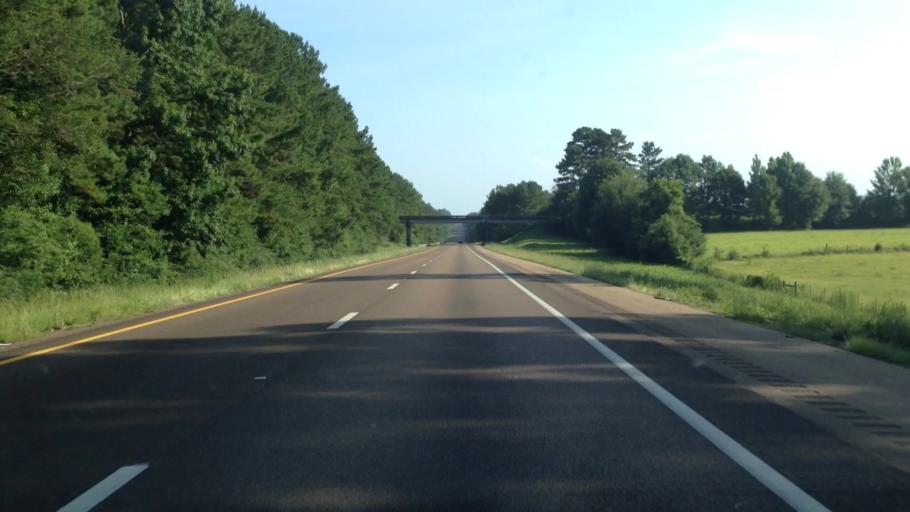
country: US
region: Mississippi
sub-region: Pike County
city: Summit
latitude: 31.3871
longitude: -90.4792
